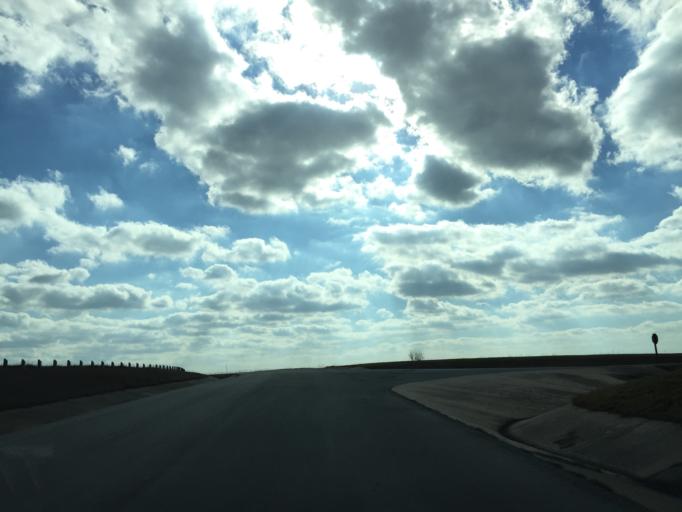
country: US
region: Texas
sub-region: Williamson County
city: Granger
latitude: 30.6803
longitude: -97.3420
